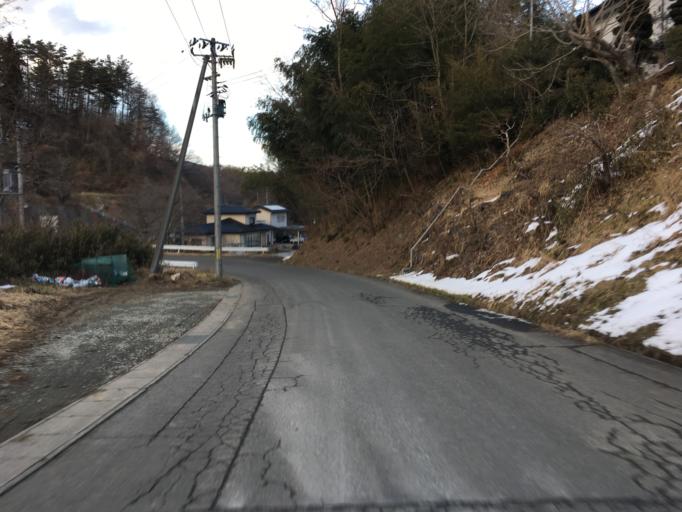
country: JP
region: Fukushima
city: Fukushima-shi
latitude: 37.6522
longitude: 140.5885
